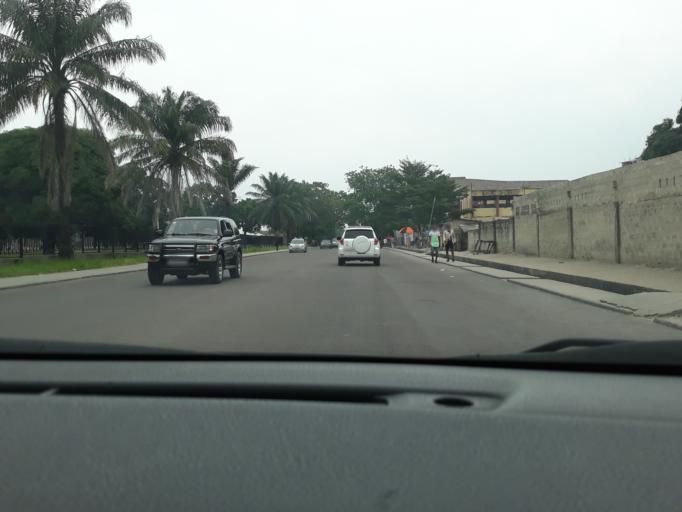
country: CD
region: Kinshasa
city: Kinshasa
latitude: -4.3301
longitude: 15.3046
